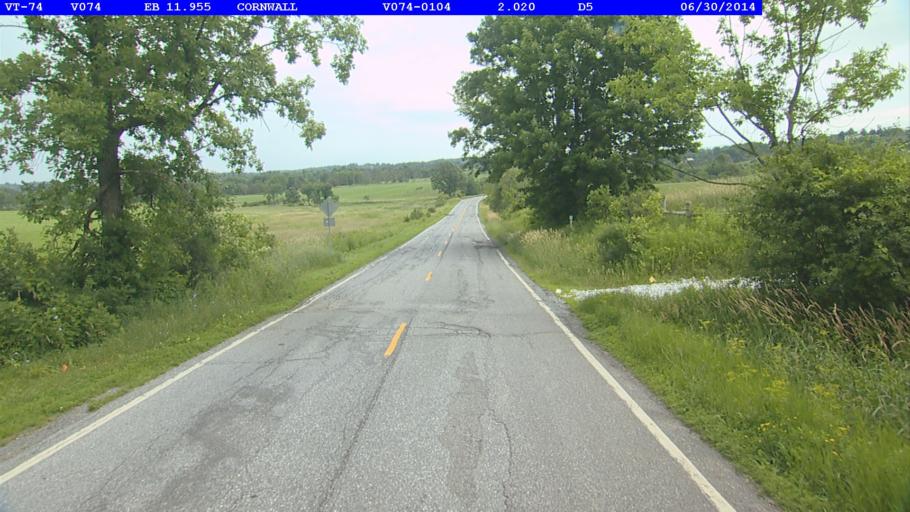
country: US
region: Vermont
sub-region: Addison County
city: Middlebury (village)
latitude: 43.9519
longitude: -73.2222
